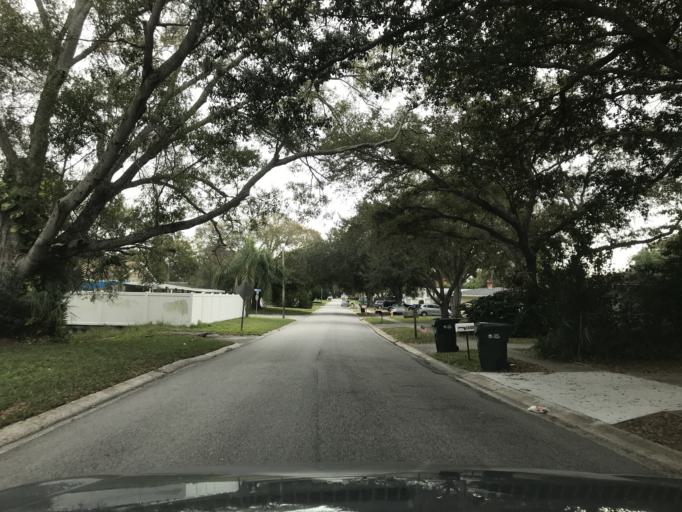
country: US
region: Florida
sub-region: Pinellas County
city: Largo
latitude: 27.9319
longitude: -82.7794
